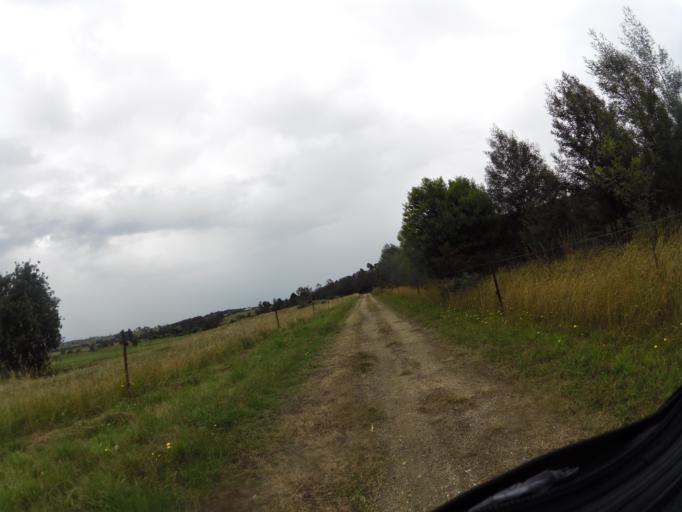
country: AU
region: Victoria
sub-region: East Gippsland
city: Lakes Entrance
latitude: -37.7060
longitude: 147.8203
